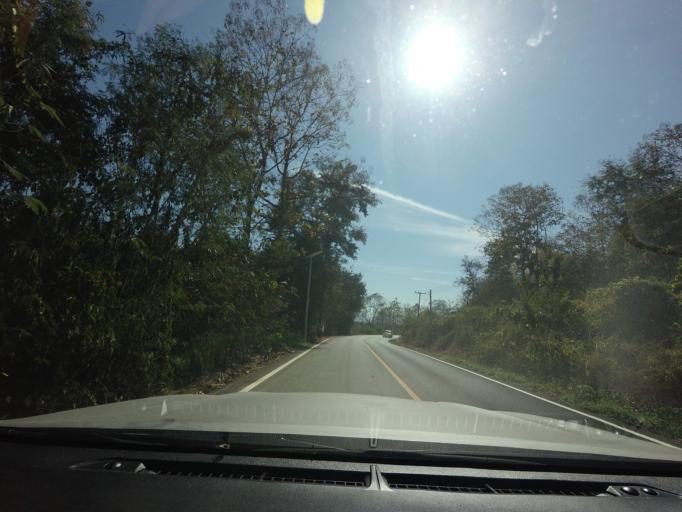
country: TH
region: Mae Hong Son
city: Wiang Nuea
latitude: 19.3765
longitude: 98.4359
